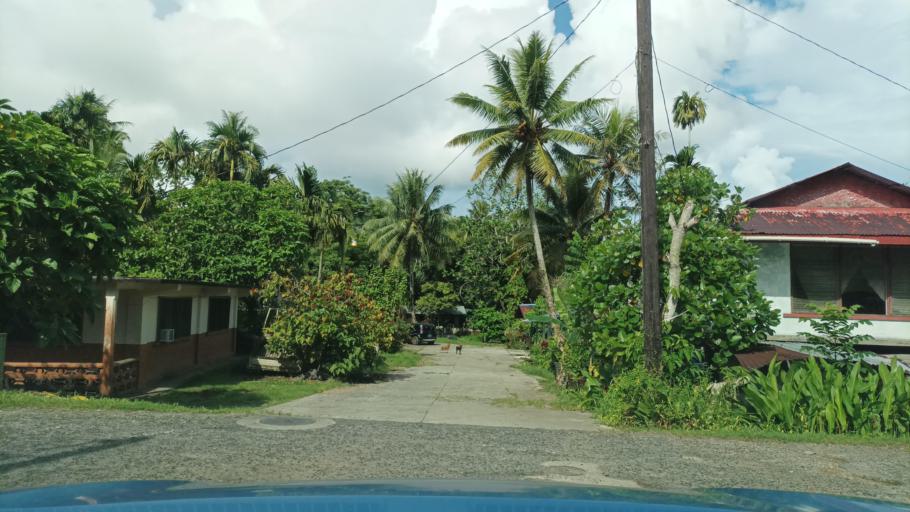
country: FM
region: Pohnpei
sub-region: Kolonia Municipality
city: Kolonia
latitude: 6.9649
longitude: 158.2096
